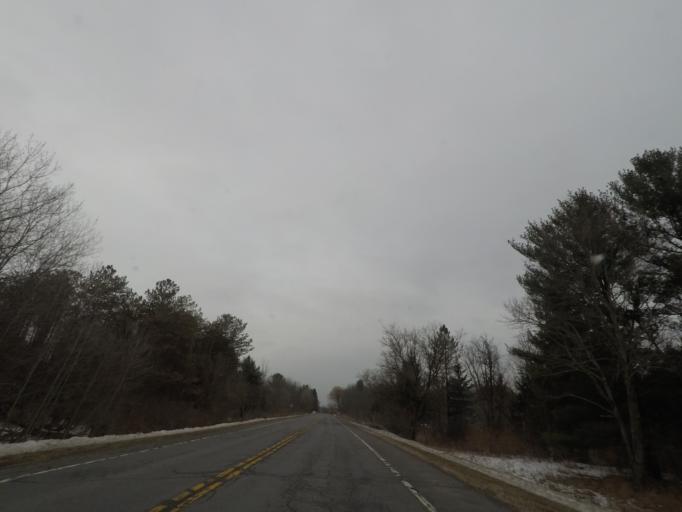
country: US
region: New York
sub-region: Schenectady County
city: Rotterdam
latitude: 42.7398
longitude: -73.9838
